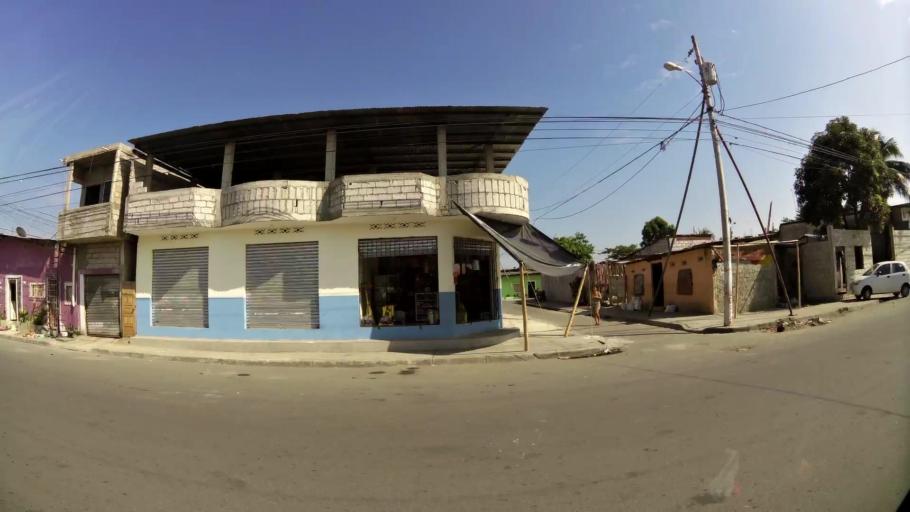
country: EC
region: Guayas
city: Eloy Alfaro
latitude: -2.1013
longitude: -79.9213
